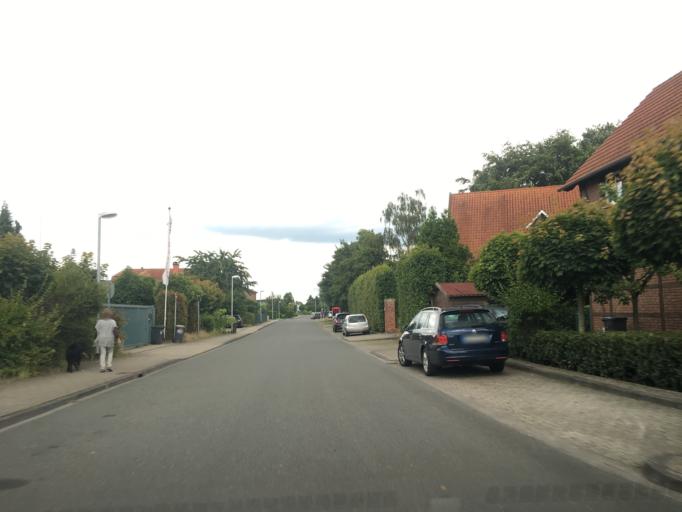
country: DE
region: North Rhine-Westphalia
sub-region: Regierungsbezirk Munster
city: Telgte
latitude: 51.9282
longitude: 7.7183
